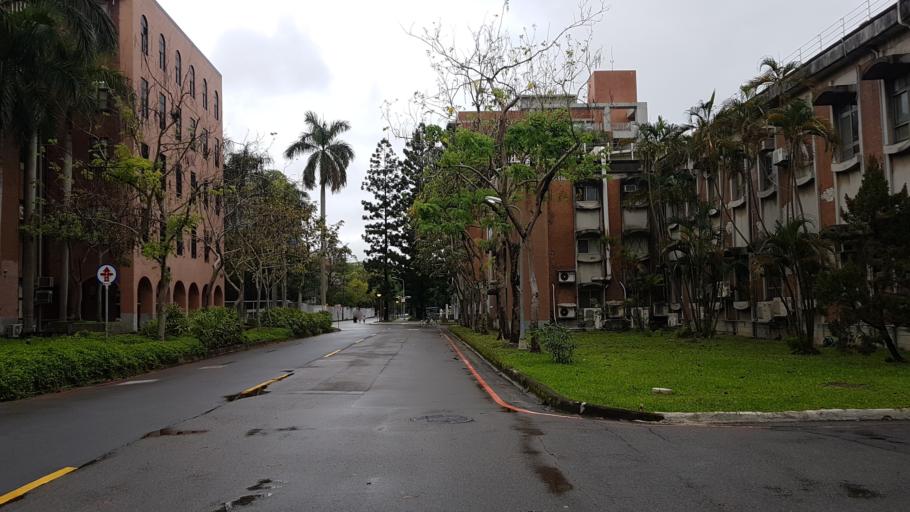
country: TW
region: Taipei
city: Taipei
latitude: 25.0184
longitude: 121.5382
